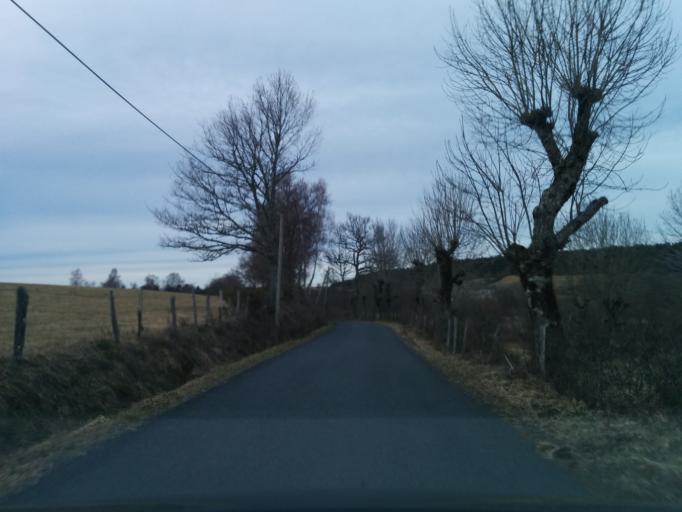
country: FR
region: Auvergne
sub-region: Departement du Cantal
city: Chaudes-Aigues
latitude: 44.8193
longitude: 2.8937
